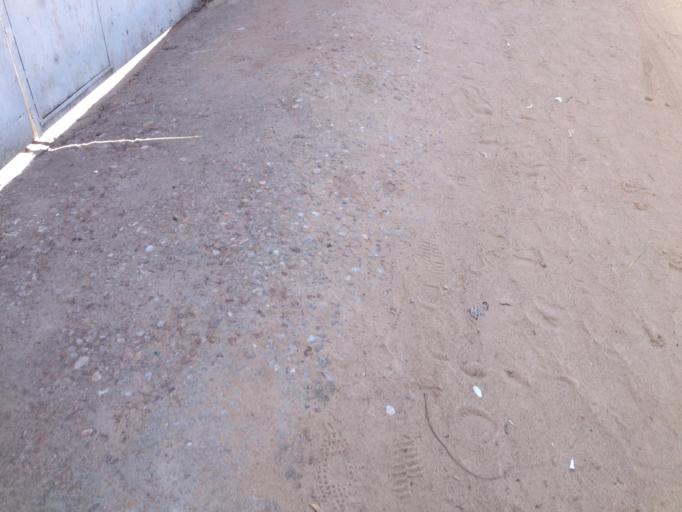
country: CD
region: Katanga
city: Kalemie
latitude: -5.9102
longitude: 29.2076
